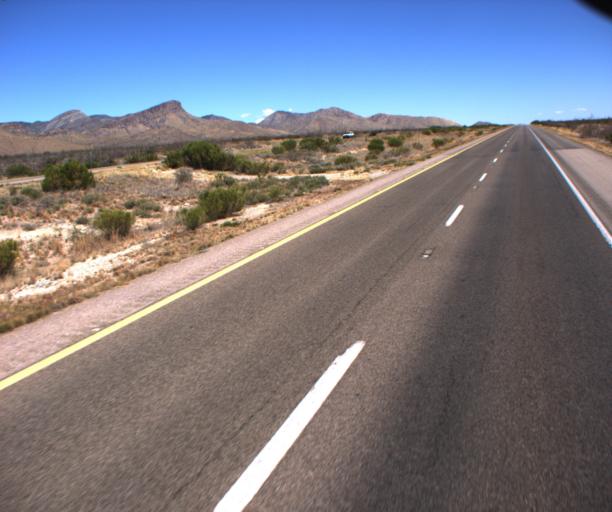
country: US
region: Arizona
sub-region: Cochise County
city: Huachuca City
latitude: 31.7703
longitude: -110.3500
